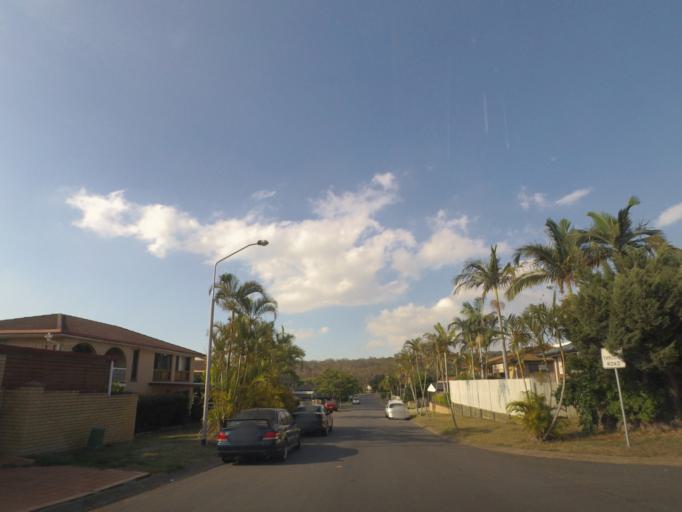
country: AU
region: Queensland
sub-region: Brisbane
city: Robertson
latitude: -27.5627
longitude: 153.0574
